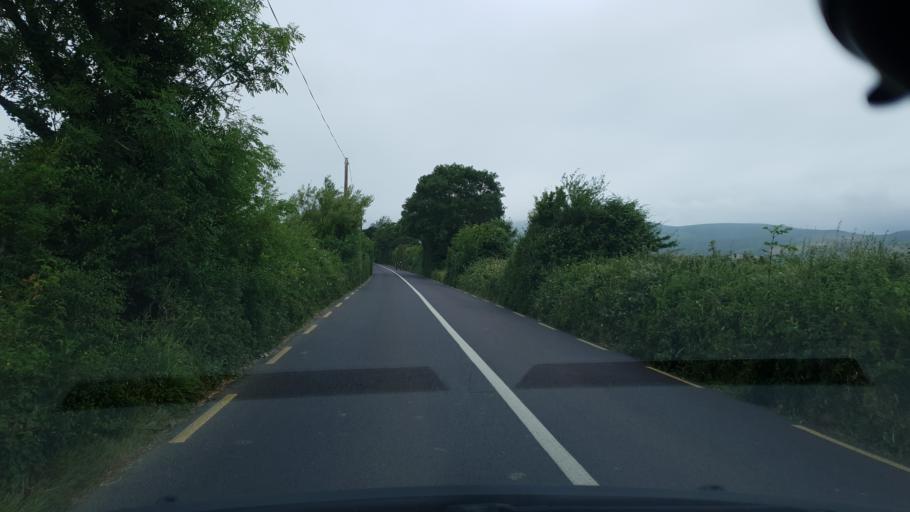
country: IE
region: Munster
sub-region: Ciarrai
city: Tralee
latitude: 52.1597
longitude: -9.6848
